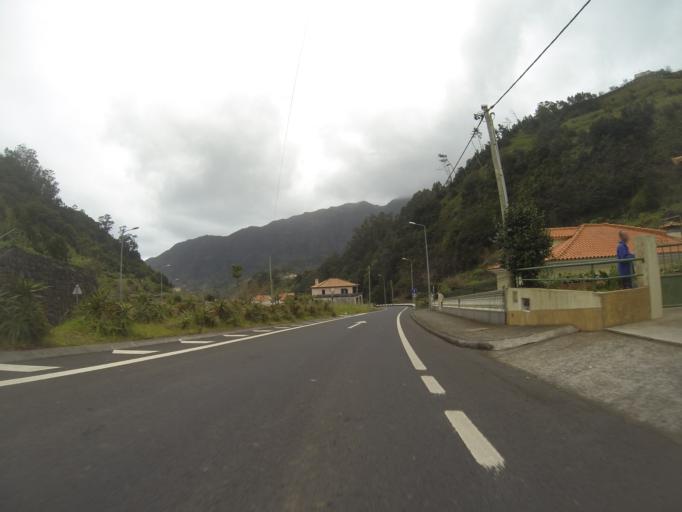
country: PT
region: Madeira
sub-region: Sao Vicente
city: Sao Vicente
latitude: 32.7825
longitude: -17.0328
